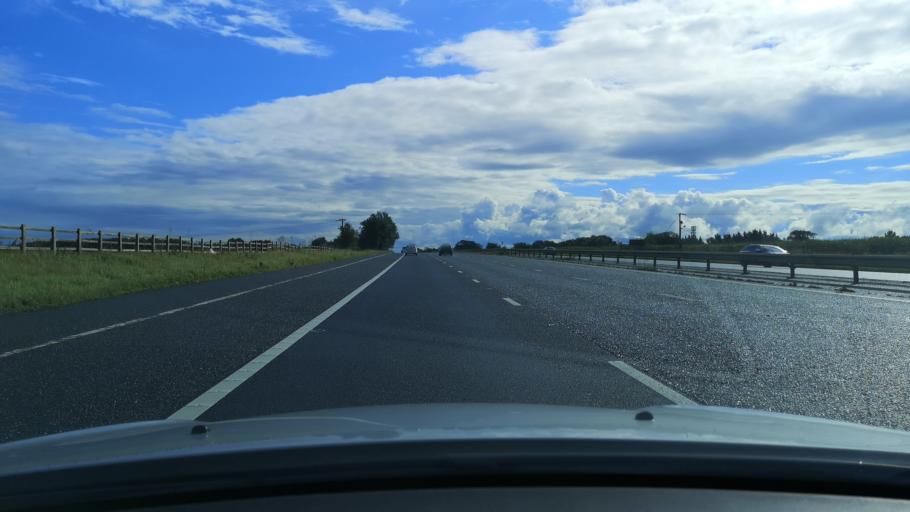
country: GB
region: England
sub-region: East Riding of Yorkshire
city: Pollington
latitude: 53.6898
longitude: -1.1061
